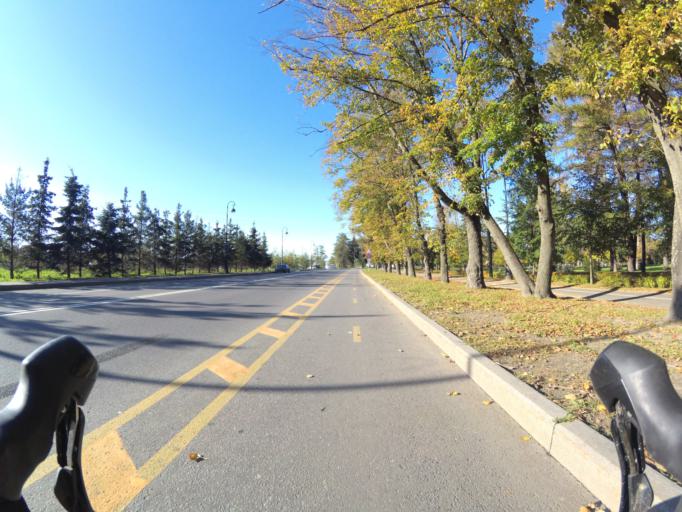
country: RU
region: Leningrad
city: Krestovskiy ostrov
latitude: 59.9679
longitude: 30.2436
